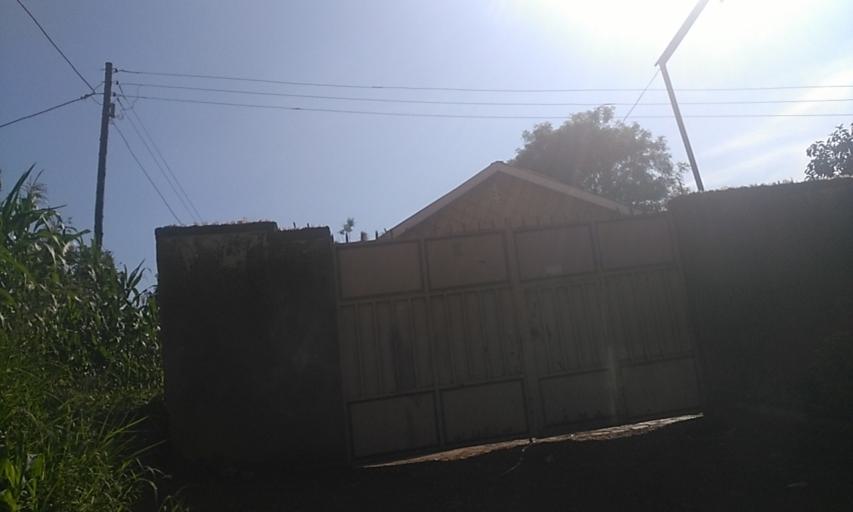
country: UG
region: Central Region
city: Kampala Central Division
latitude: 0.3186
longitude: 32.5495
